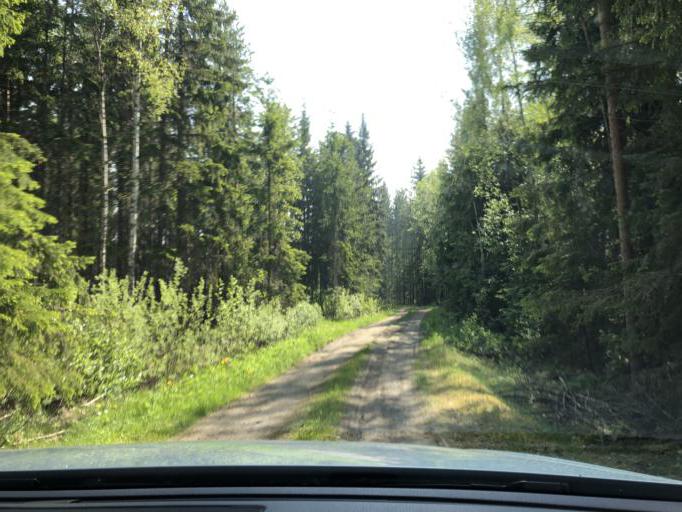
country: SE
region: Dalarna
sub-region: Avesta Kommun
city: Horndal
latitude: 60.2161
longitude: 16.4930
